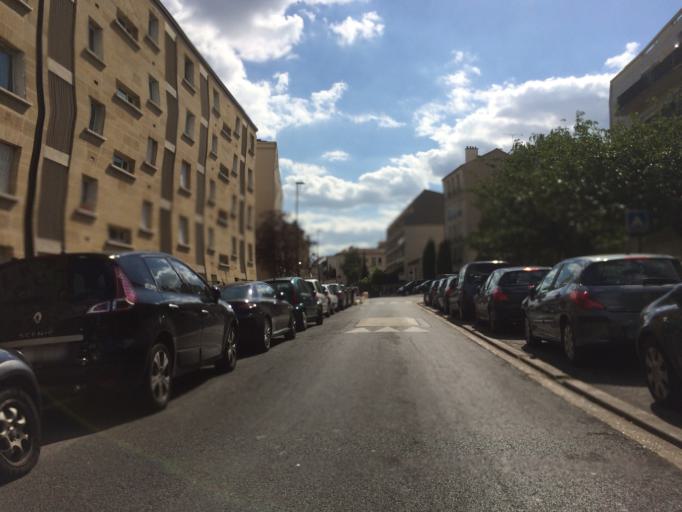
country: FR
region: Ile-de-France
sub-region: Departement des Hauts-de-Seine
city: Suresnes
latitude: 48.8769
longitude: 2.2285
